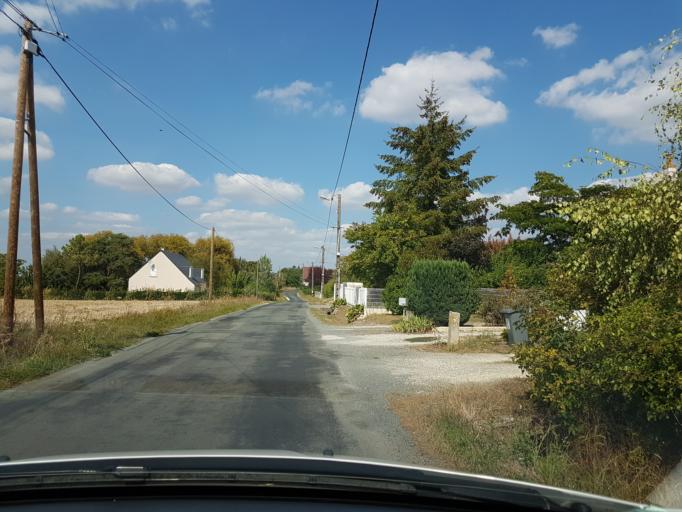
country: FR
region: Centre
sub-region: Departement d'Indre-et-Loire
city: Larcay
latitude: 47.3612
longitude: 0.7816
